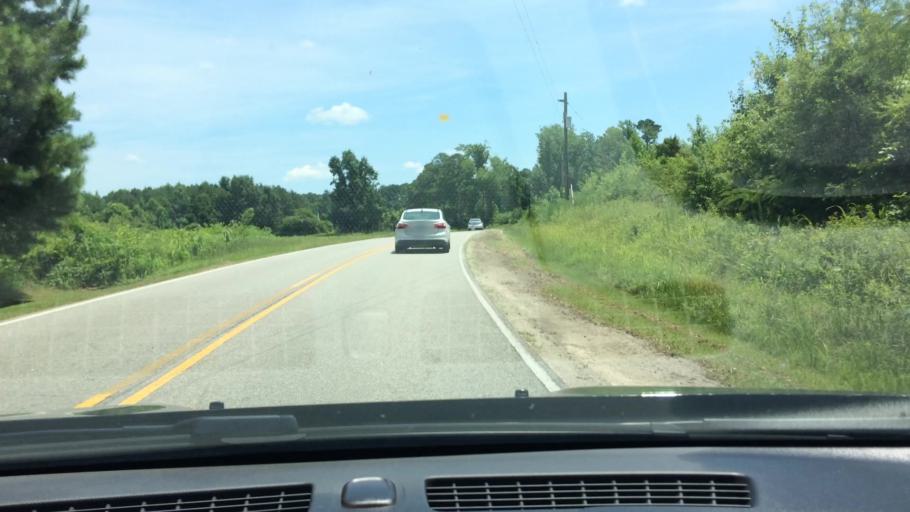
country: US
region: North Carolina
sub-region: Beaufort County
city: Washington
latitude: 35.5671
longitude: -77.2053
